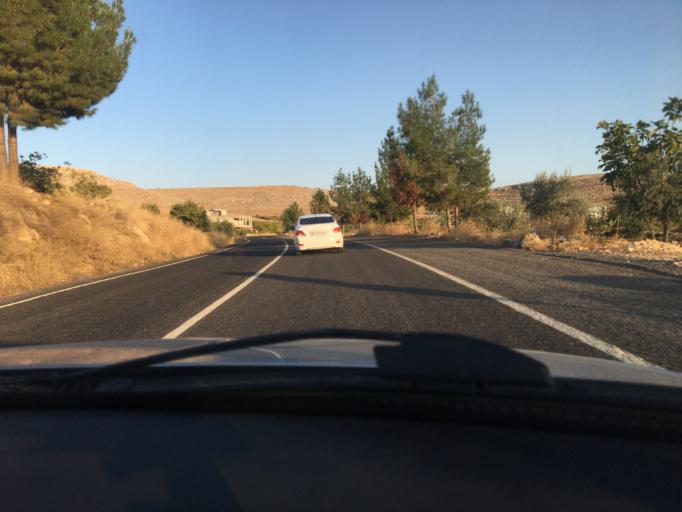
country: TR
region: Sanliurfa
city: Halfeti
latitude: 37.2158
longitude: 37.9577
